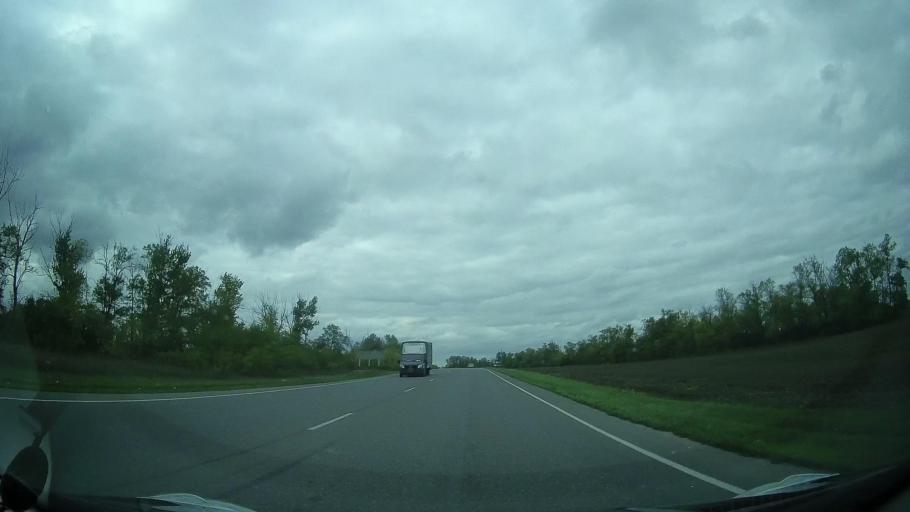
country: RU
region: Rostov
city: Mechetinskaya
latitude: 46.7500
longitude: 40.4623
